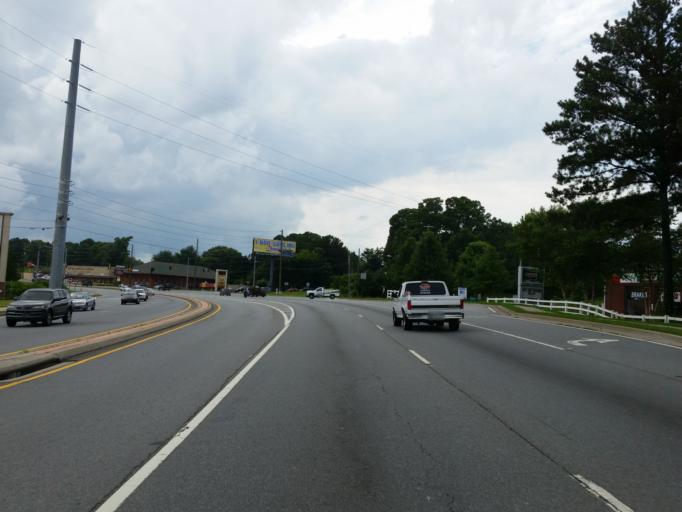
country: US
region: Georgia
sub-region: Cherokee County
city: Woodstock
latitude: 34.0869
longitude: -84.5447
